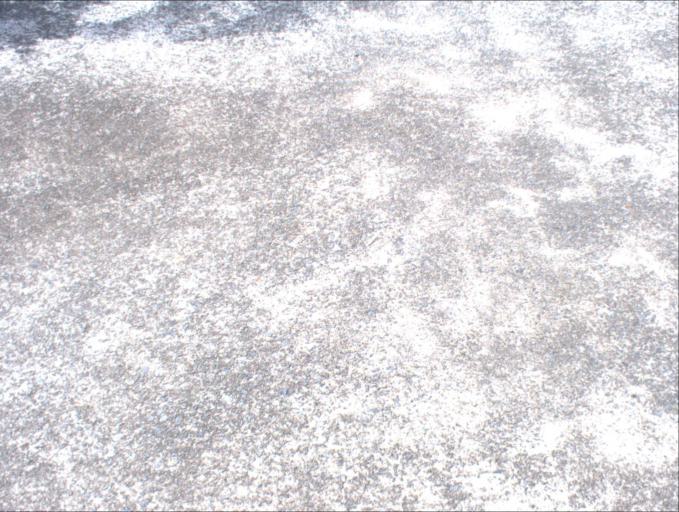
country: AU
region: Queensland
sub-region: Logan
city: Waterford West
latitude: -27.6826
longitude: 153.1051
